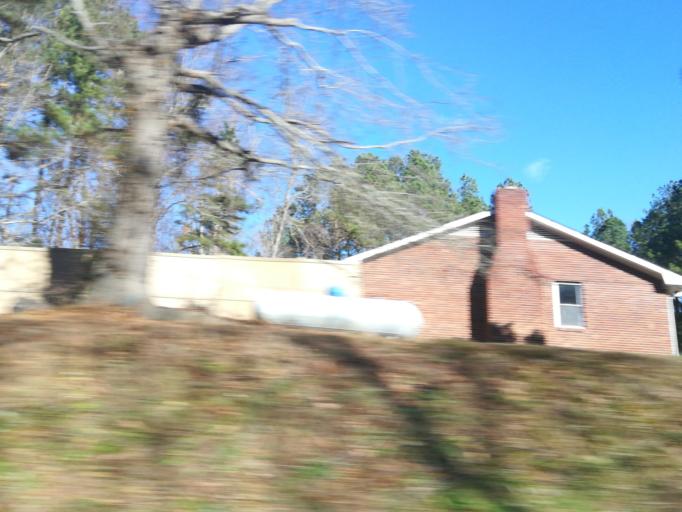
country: US
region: North Carolina
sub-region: Durham County
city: Durham
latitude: 36.0333
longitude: -78.9942
